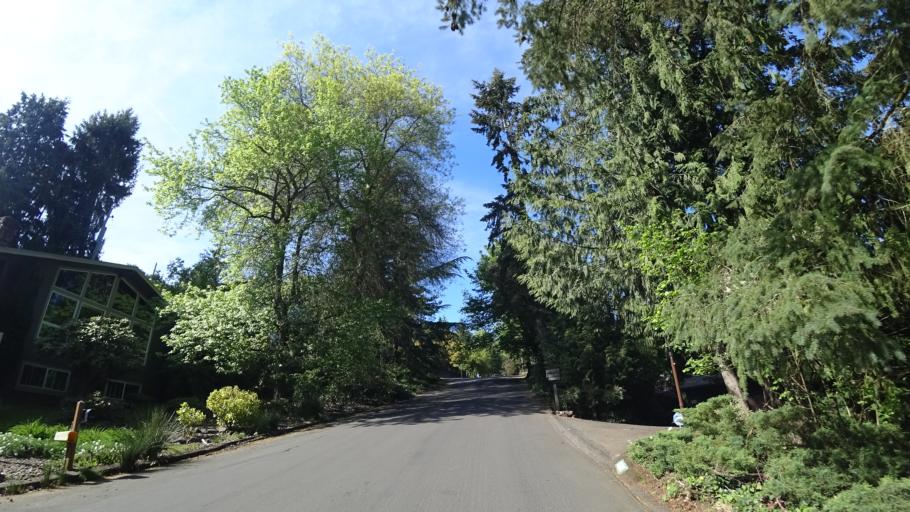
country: US
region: Oregon
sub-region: Washington County
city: West Slope
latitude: 45.4937
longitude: -122.7485
